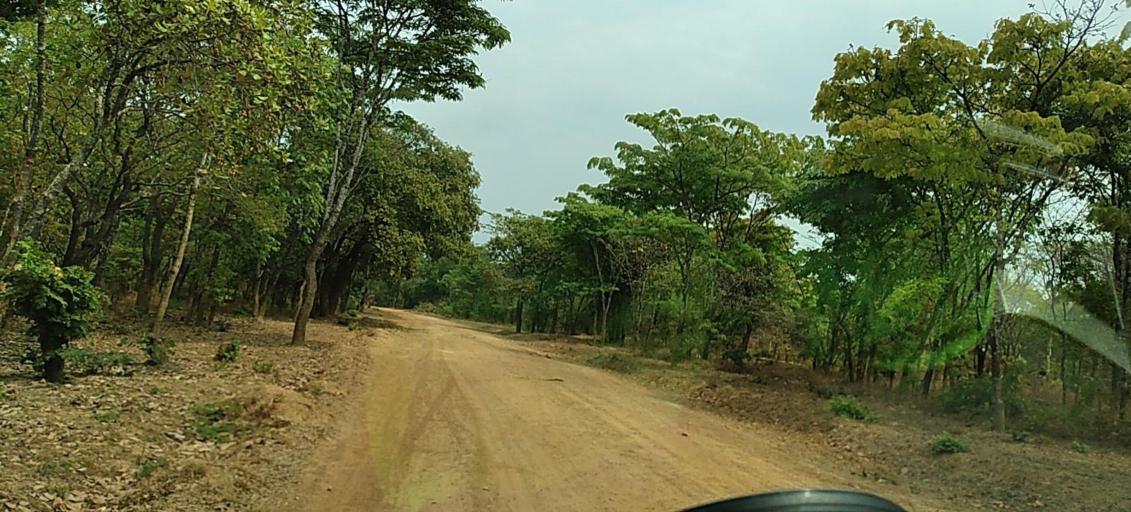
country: ZM
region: North-Western
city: Solwezi
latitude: -12.9615
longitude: 26.5685
